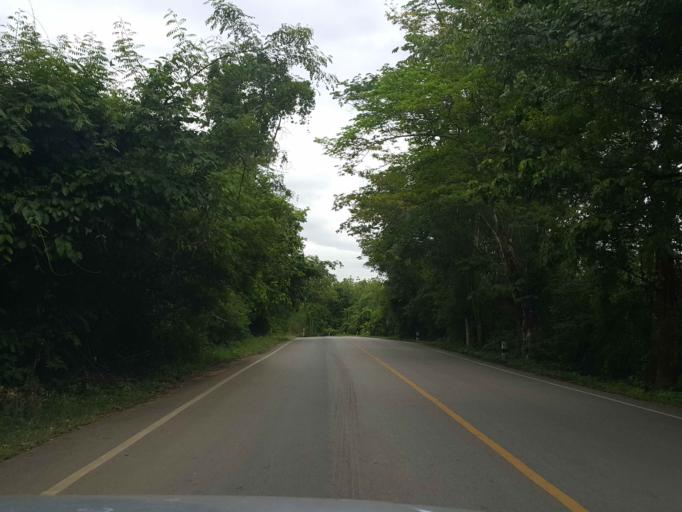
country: TH
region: Sukhothai
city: Thung Saliam
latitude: 17.3495
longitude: 99.4355
